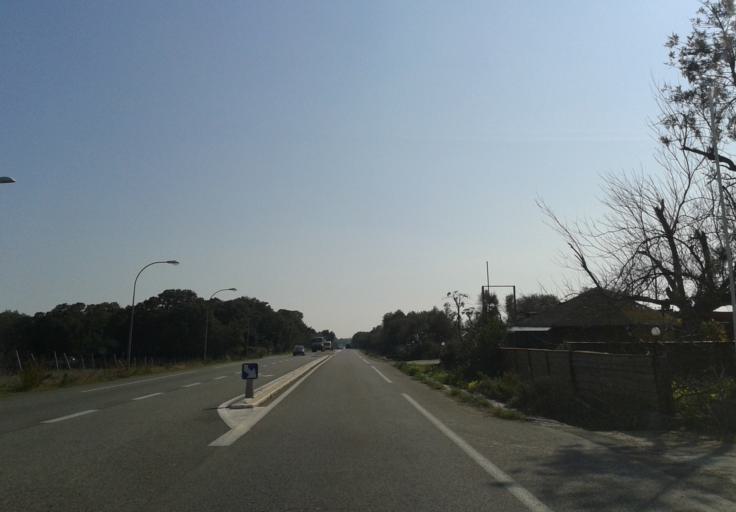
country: FR
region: Corsica
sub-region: Departement de la Haute-Corse
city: Linguizzetta
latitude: 42.2775
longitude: 9.5501
